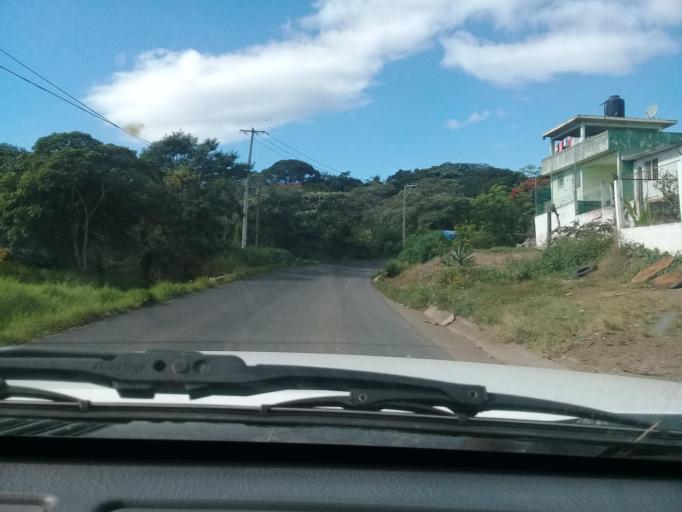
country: MX
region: Veracruz
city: El Castillo
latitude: 19.5471
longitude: -96.8827
